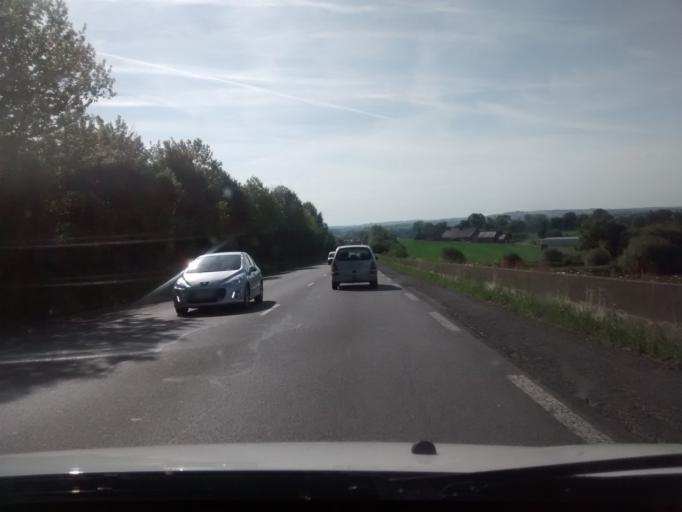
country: FR
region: Brittany
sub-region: Departement d'Ille-et-Vilaine
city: Lecousse
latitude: 48.3446
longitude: -1.2241
